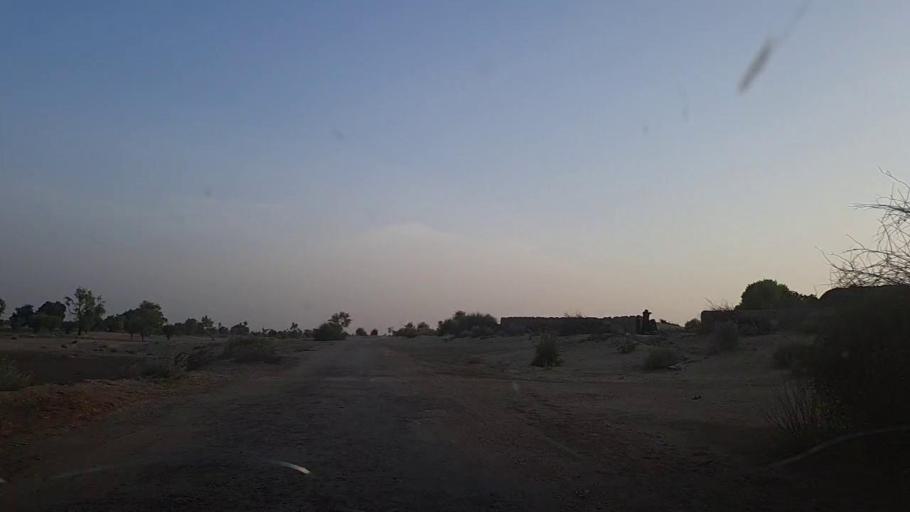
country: PK
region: Sindh
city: Khanpur
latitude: 27.5973
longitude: 69.4266
